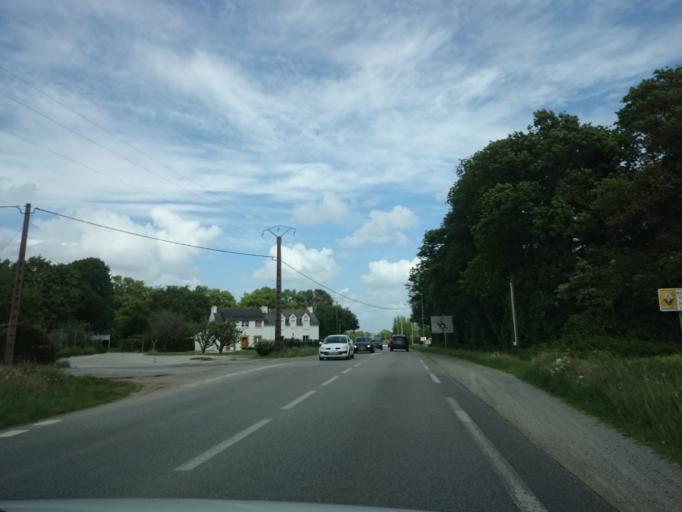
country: FR
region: Brittany
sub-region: Departement du Morbihan
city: Arradon
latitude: 47.6425
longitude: -2.8176
